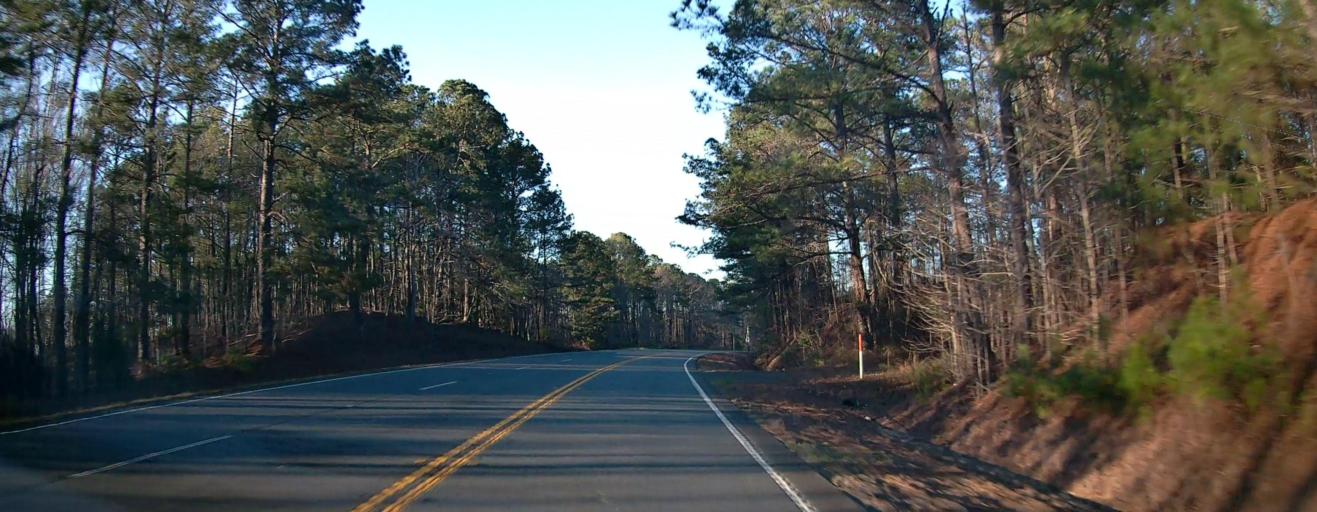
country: US
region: Georgia
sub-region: Talbot County
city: Talbotton
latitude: 32.6481
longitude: -84.5399
